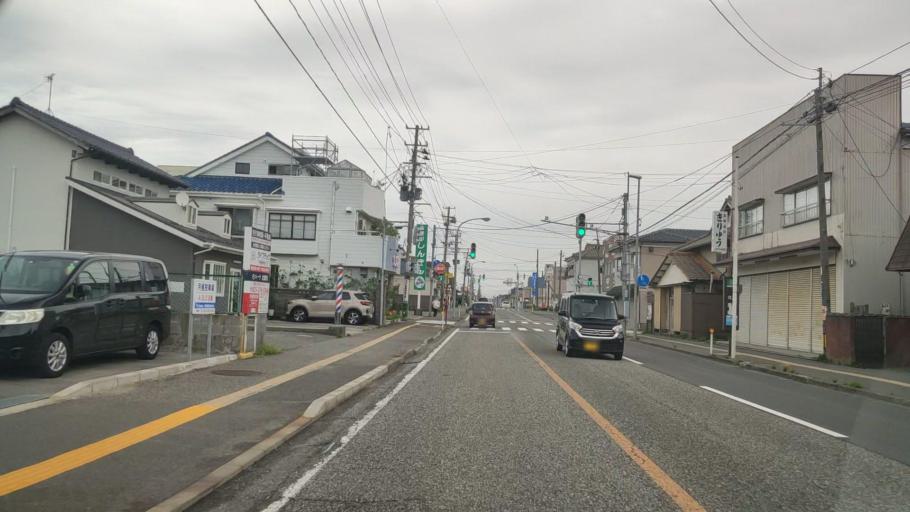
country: JP
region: Niigata
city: Niigata-shi
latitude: 37.9392
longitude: 139.0760
